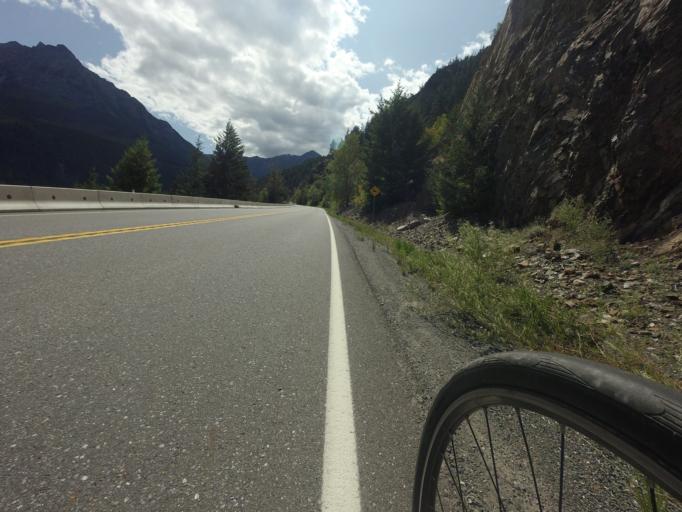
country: CA
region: British Columbia
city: Lillooet
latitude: 50.6577
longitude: -121.9967
